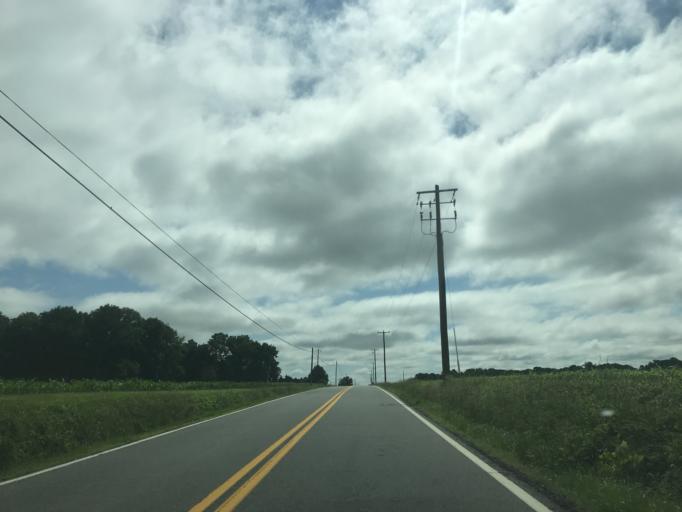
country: US
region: Maryland
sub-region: Caroline County
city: Ridgely
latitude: 38.8856
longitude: -75.9667
